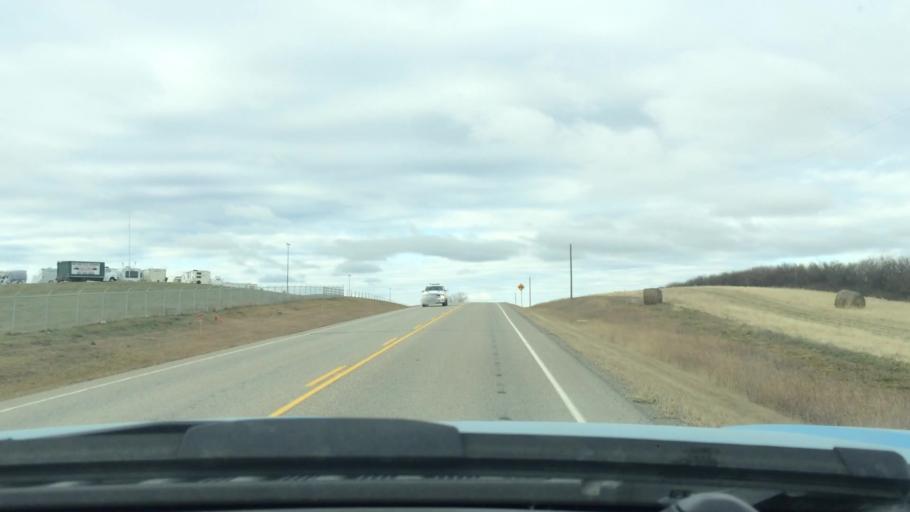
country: CA
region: Alberta
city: Airdrie
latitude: 51.2126
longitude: -114.0493
